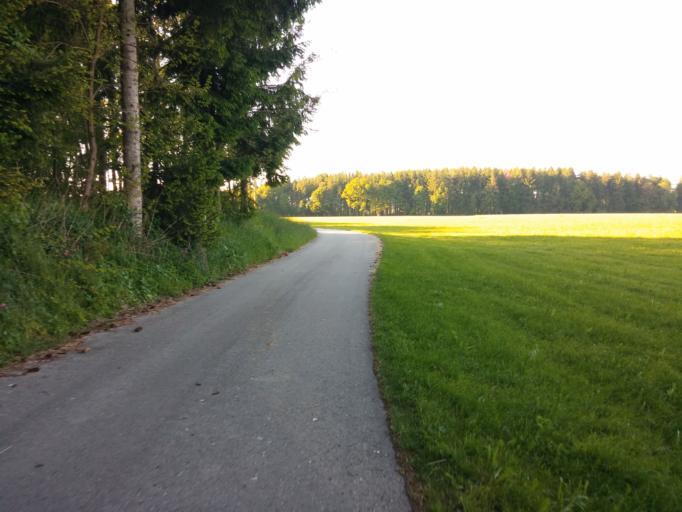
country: DE
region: Bavaria
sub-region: Swabia
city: Legau
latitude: 47.8632
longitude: 10.1698
